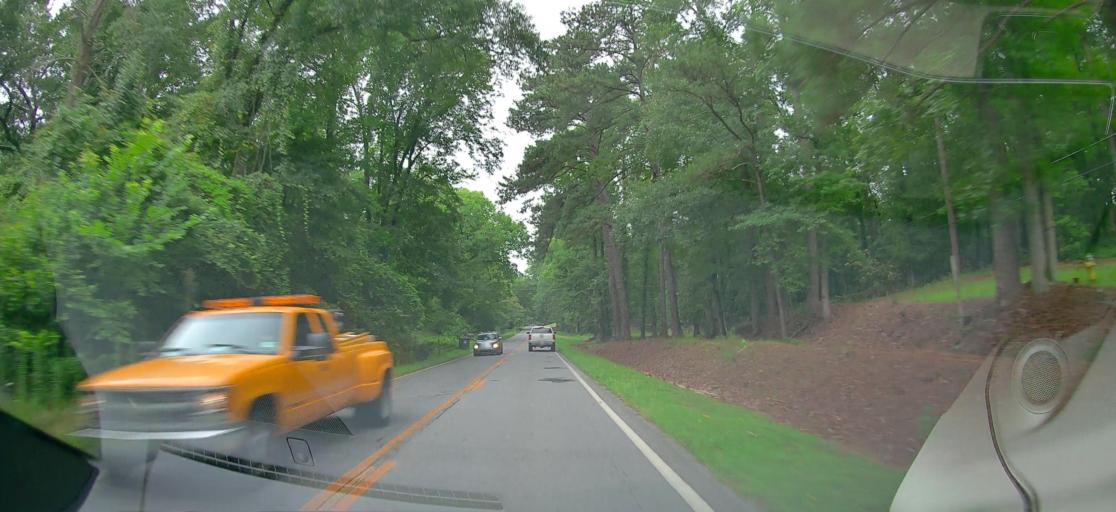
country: US
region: Georgia
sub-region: Peach County
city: Byron
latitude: 32.7168
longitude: -83.7383
